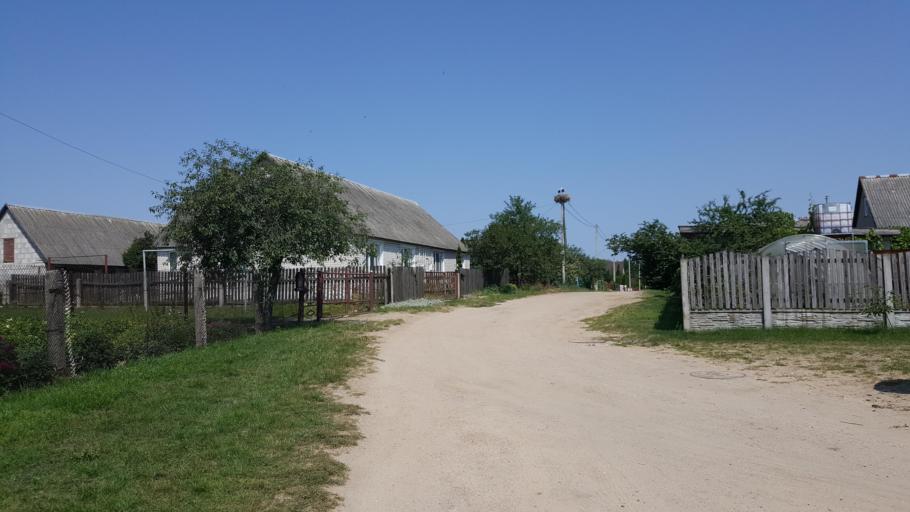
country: BY
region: Brest
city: Zhabinka
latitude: 52.1973
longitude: 23.9931
